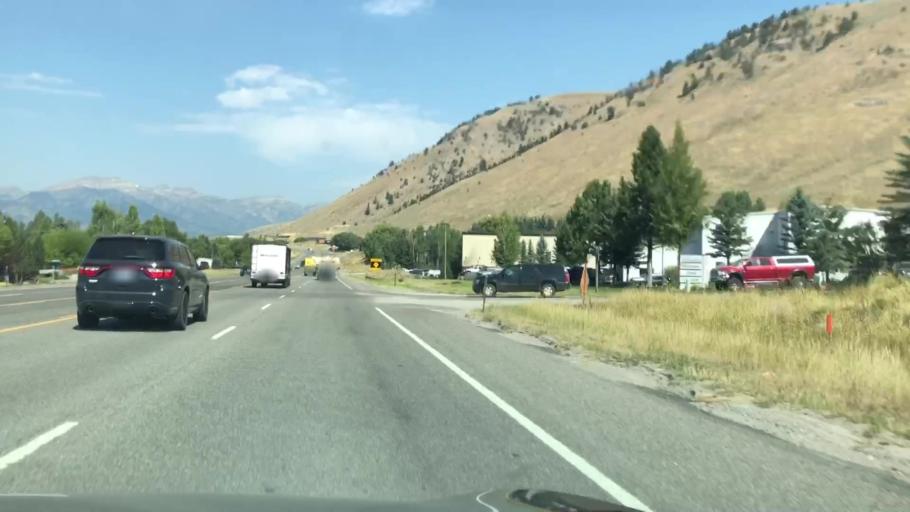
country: US
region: Wyoming
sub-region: Teton County
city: South Park
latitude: 43.4227
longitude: -110.7768
